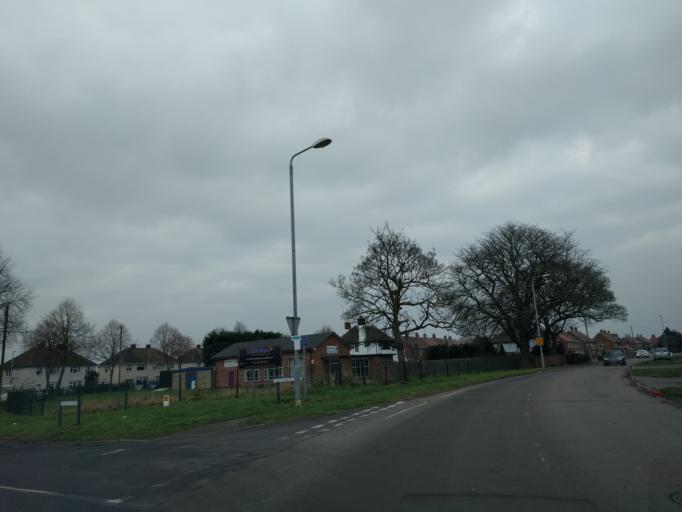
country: GB
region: England
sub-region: Nottinghamshire
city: Newark on Trent
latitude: 53.0869
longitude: -0.7996
